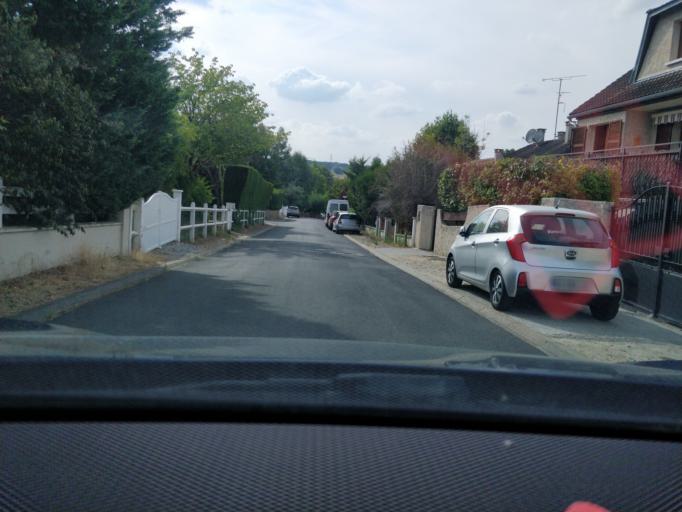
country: FR
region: Ile-de-France
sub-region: Departement de l'Essonne
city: Briis-sous-Forges
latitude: 48.6297
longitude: 2.1229
